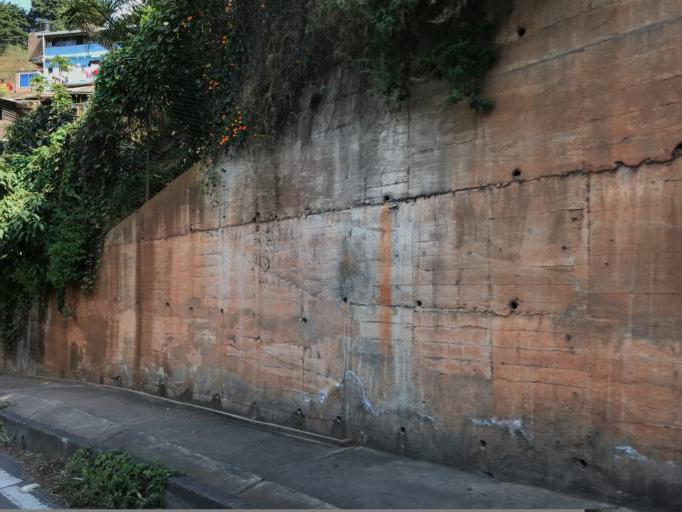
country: CO
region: Valle del Cauca
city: Cali
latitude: 3.4825
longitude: -76.6059
